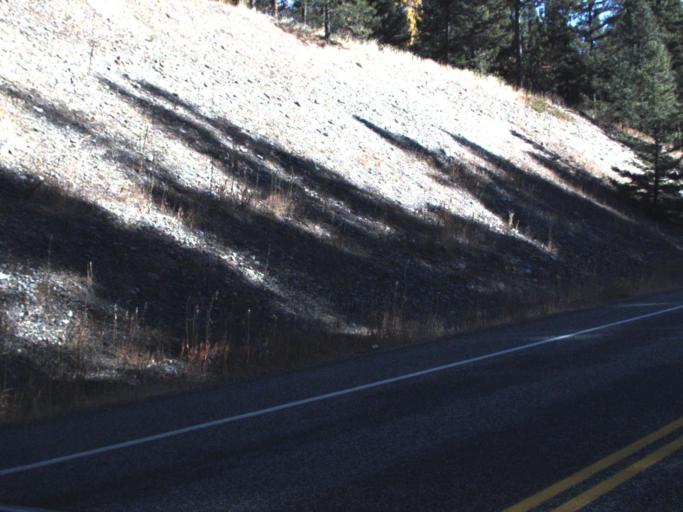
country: US
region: Washington
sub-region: Ferry County
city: Republic
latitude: 48.6562
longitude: -118.8088
